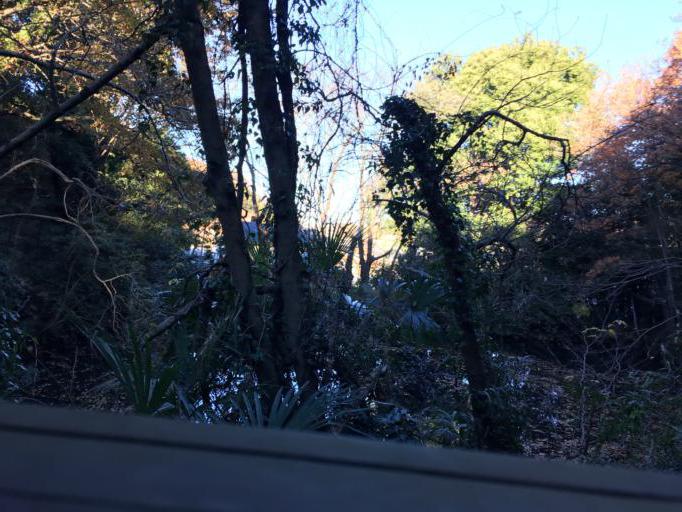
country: JP
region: Kanagawa
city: Yokohama
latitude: 35.5171
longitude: 139.6438
